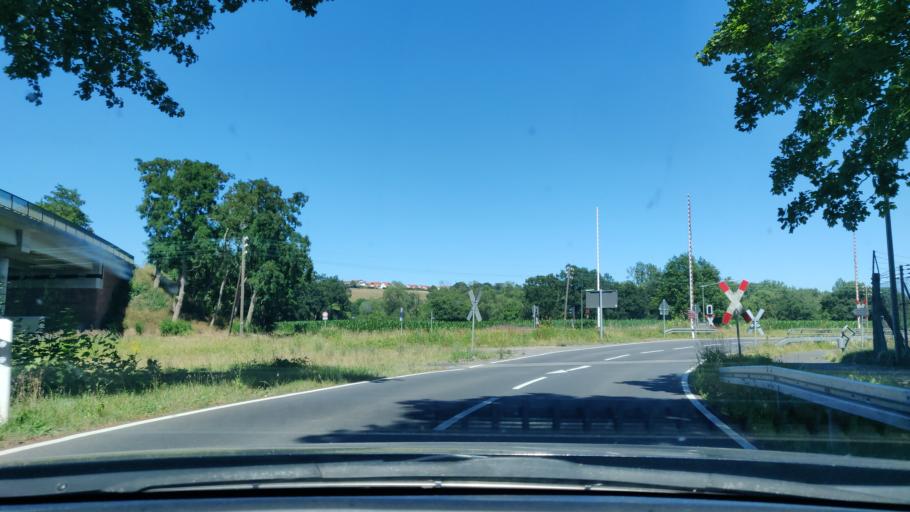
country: DE
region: Hesse
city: Fritzlar
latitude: 51.1246
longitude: 9.2896
